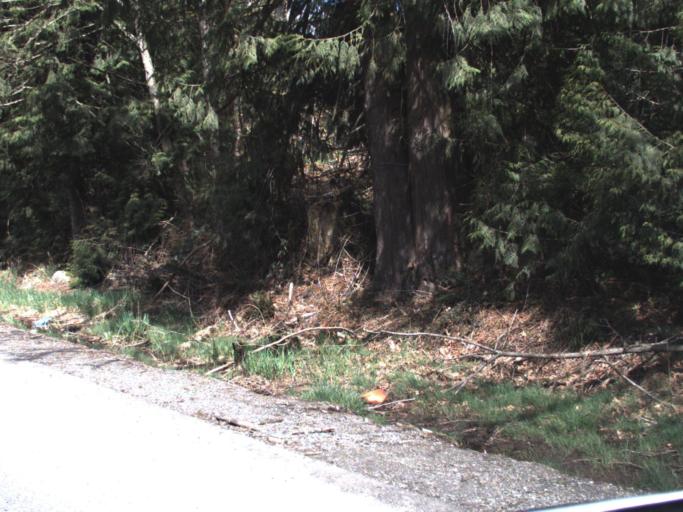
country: US
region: Washington
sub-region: King County
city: Black Diamond
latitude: 47.2934
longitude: -121.9973
